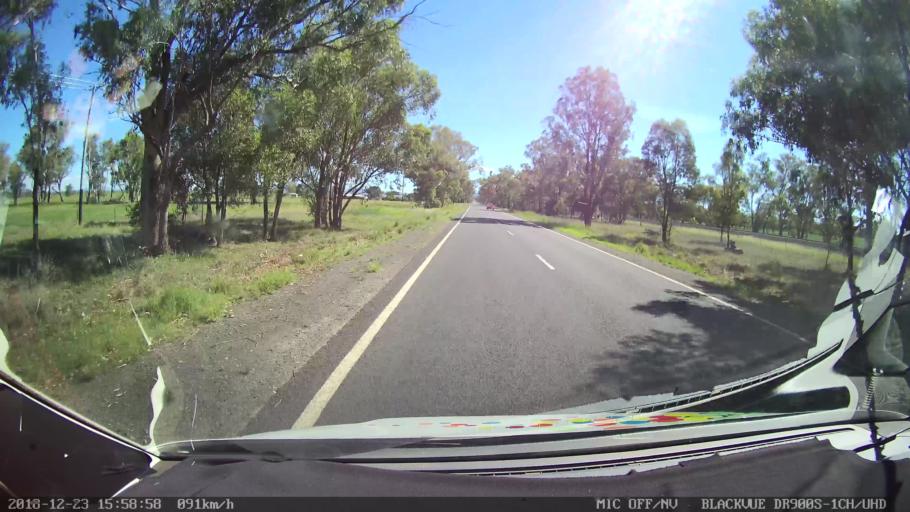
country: AU
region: New South Wales
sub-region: Tamworth Municipality
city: Phillip
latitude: -31.1943
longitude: 150.8372
